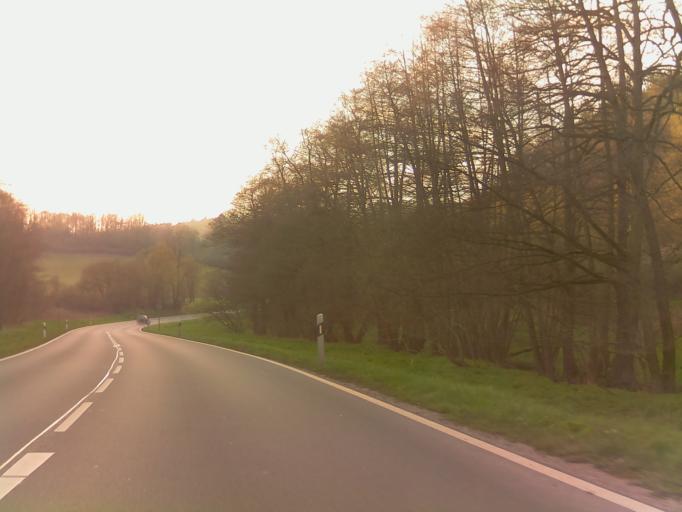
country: DE
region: Thuringia
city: Unterbreizbach
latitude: 50.8597
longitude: 9.9433
